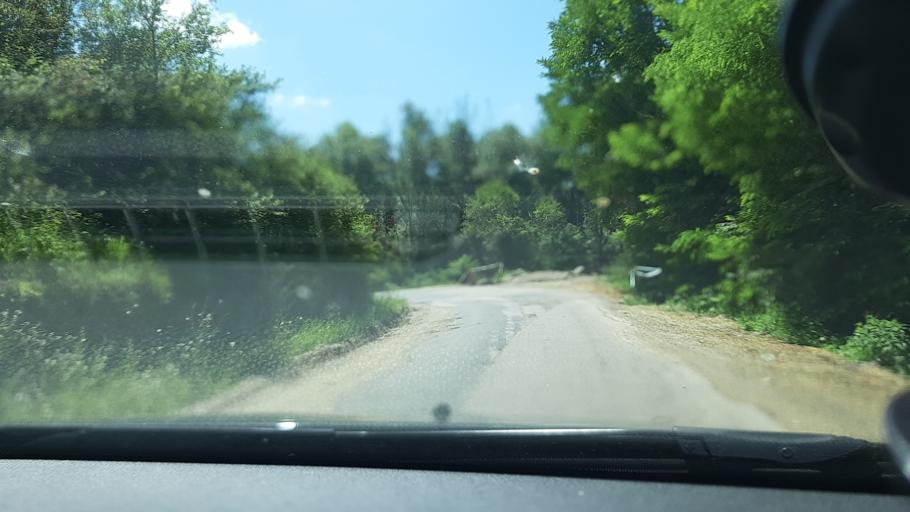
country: RO
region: Hunedoara
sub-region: Comuna Teliucu Inferior
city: Teliucu Inferior
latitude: 45.6845
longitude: 22.8729
